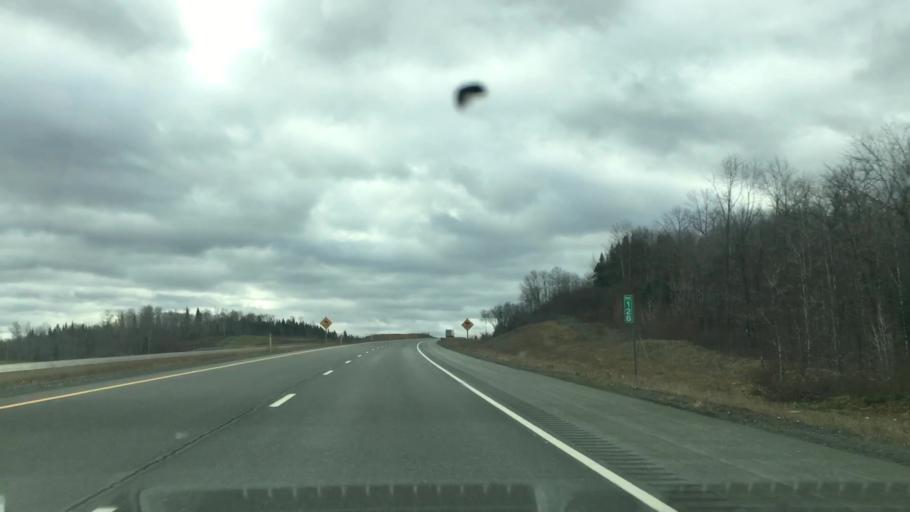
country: US
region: Maine
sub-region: Aroostook County
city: Fort Fairfield
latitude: 46.6631
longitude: -67.7321
